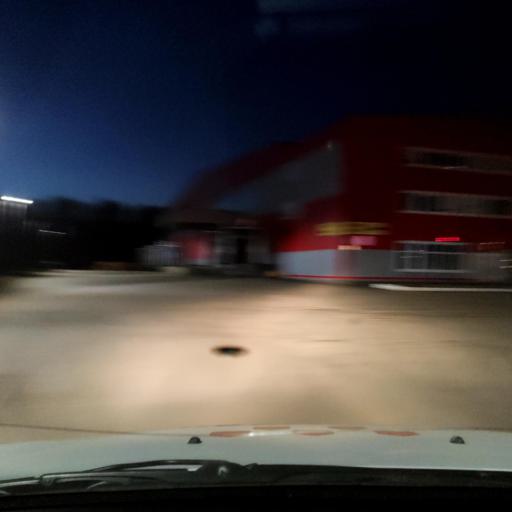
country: RU
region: Bashkortostan
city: Iglino
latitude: 54.7732
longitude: 56.2654
